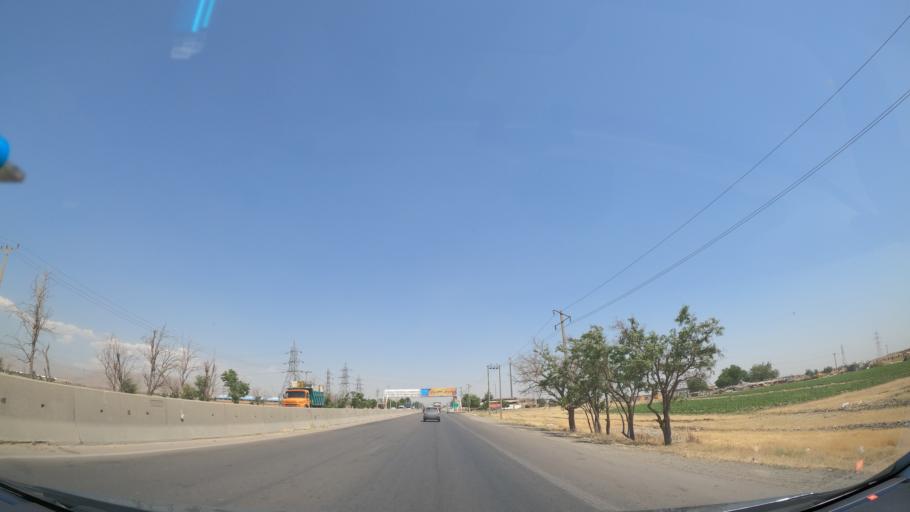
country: IR
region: Alborz
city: Hashtgerd
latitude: 35.9244
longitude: 50.7398
